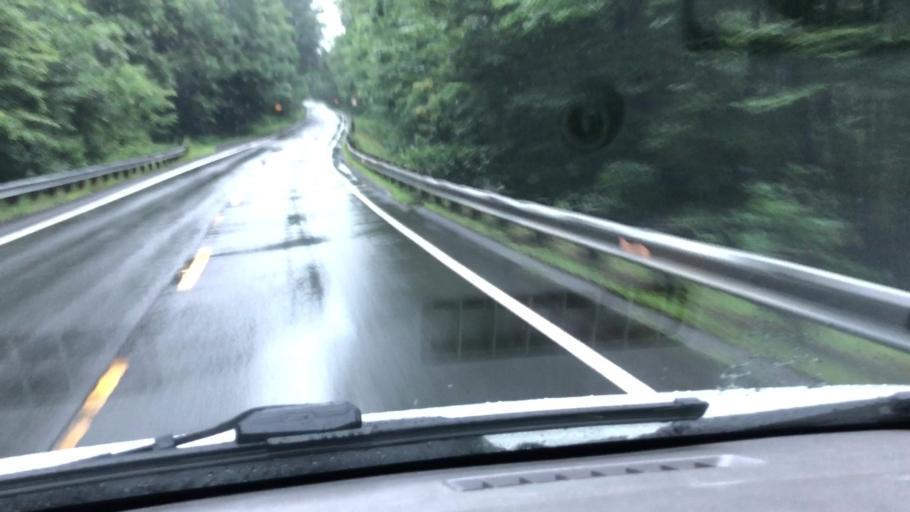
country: US
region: Massachusetts
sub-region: Hampshire County
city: Chesterfield
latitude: 42.3105
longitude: -72.8628
